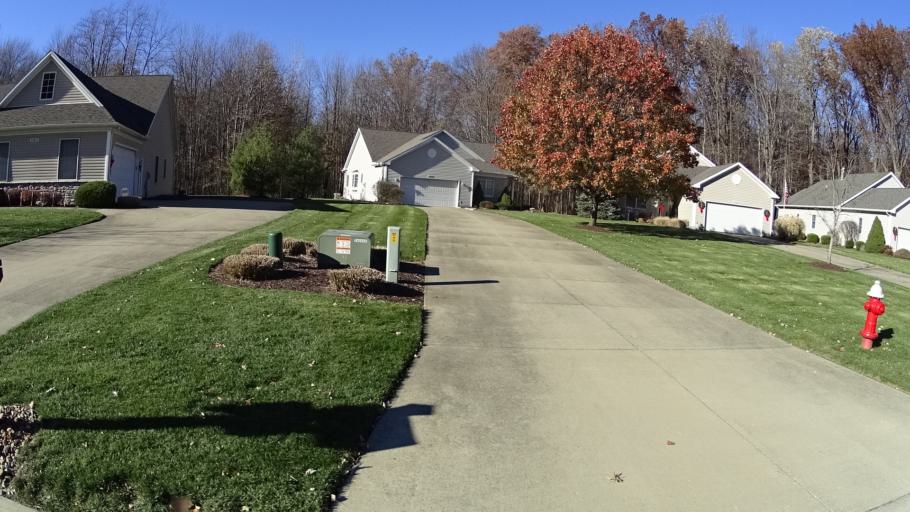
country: US
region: Ohio
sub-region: Lorain County
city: Avon Center
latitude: 41.4343
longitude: -81.9949
